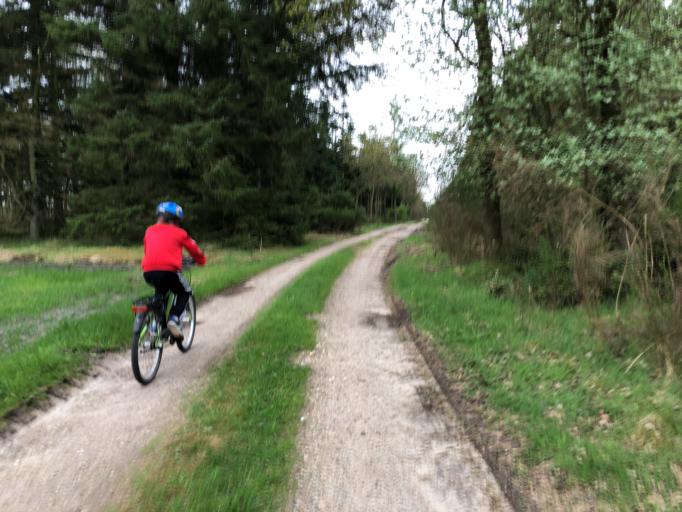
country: DK
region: Central Jutland
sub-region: Holstebro Kommune
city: Ulfborg
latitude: 56.2951
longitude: 8.4240
